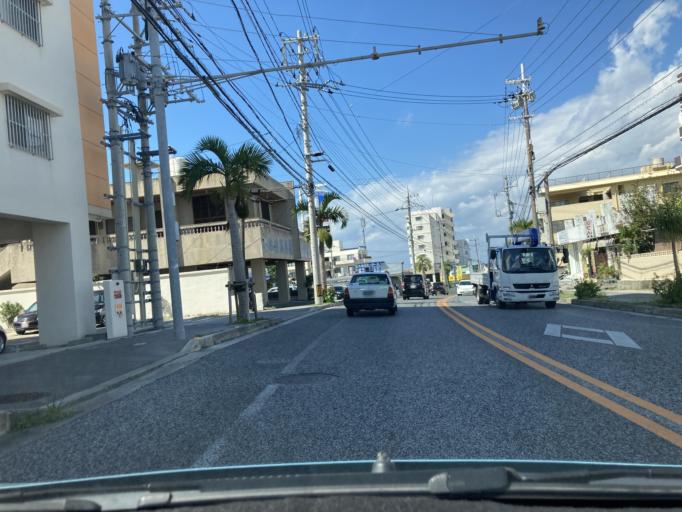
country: JP
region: Okinawa
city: Ginowan
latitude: 26.2632
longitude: 127.7401
